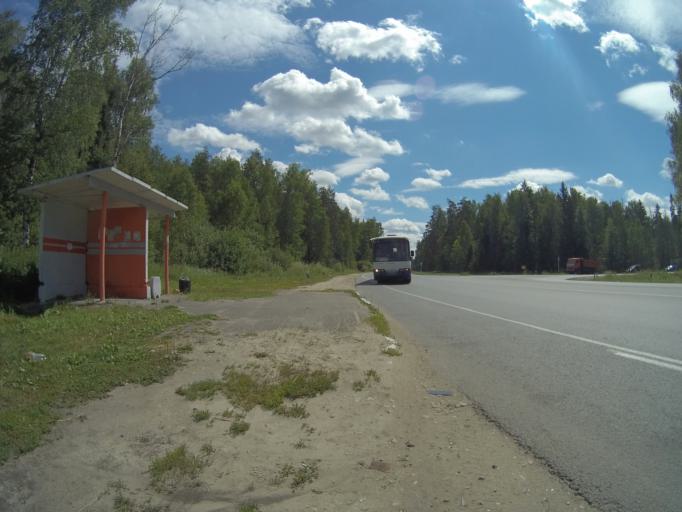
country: RU
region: Vladimir
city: Kommunar
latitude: 56.0193
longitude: 40.5811
